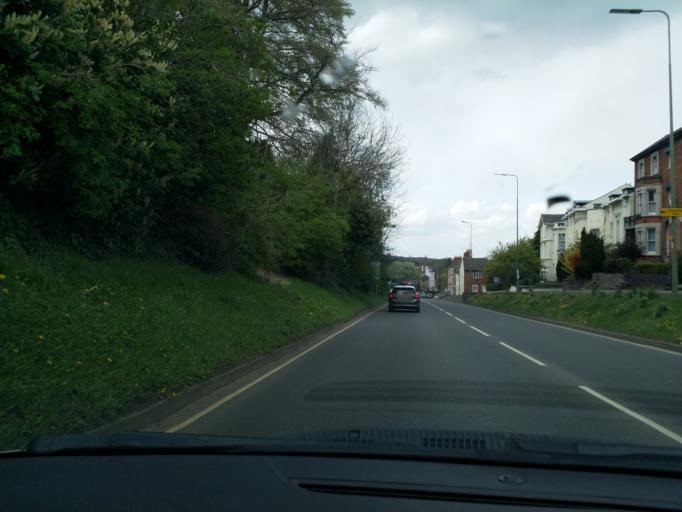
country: GB
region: England
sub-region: Oxfordshire
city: Banbury
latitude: 52.0562
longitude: -1.3396
